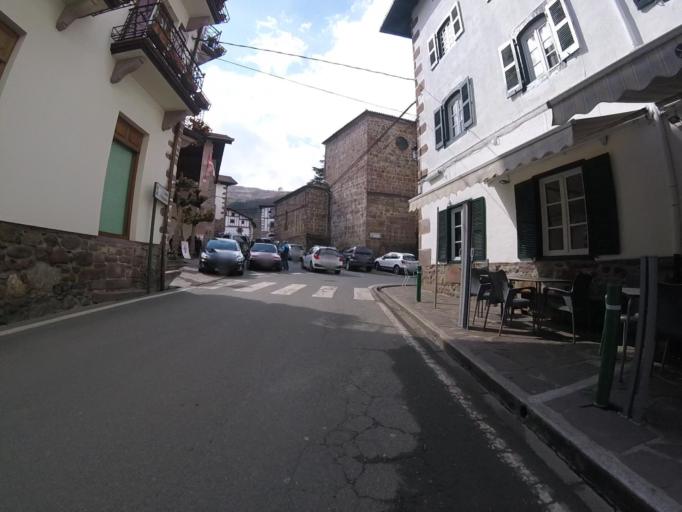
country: ES
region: Navarre
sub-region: Provincia de Navarra
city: Etxalar
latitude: 43.2341
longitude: -1.6369
